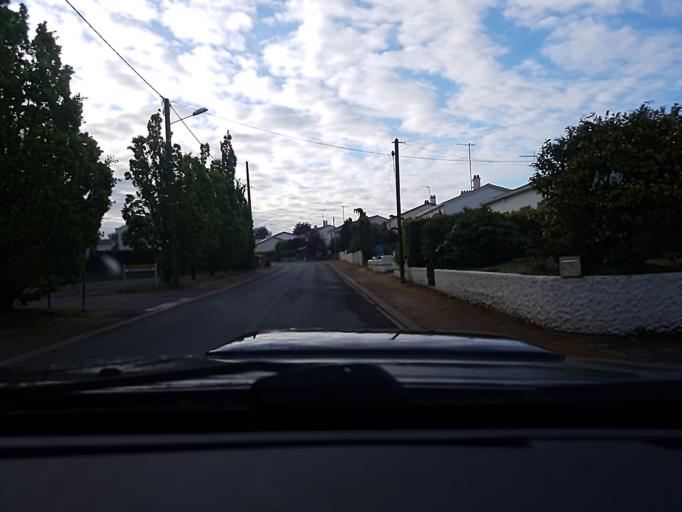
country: FR
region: Pays de la Loire
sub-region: Departement de la Vendee
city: Aizenay
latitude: 46.7419
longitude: -1.6160
